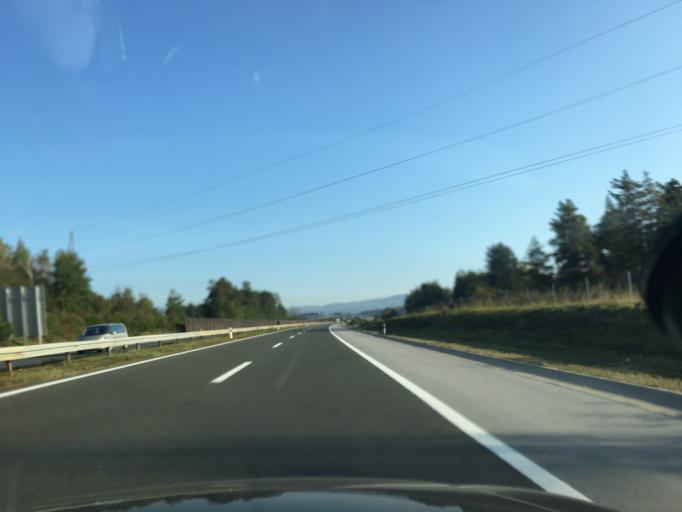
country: HR
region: Licko-Senjska
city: Gospic
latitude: 44.5798
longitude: 15.4288
